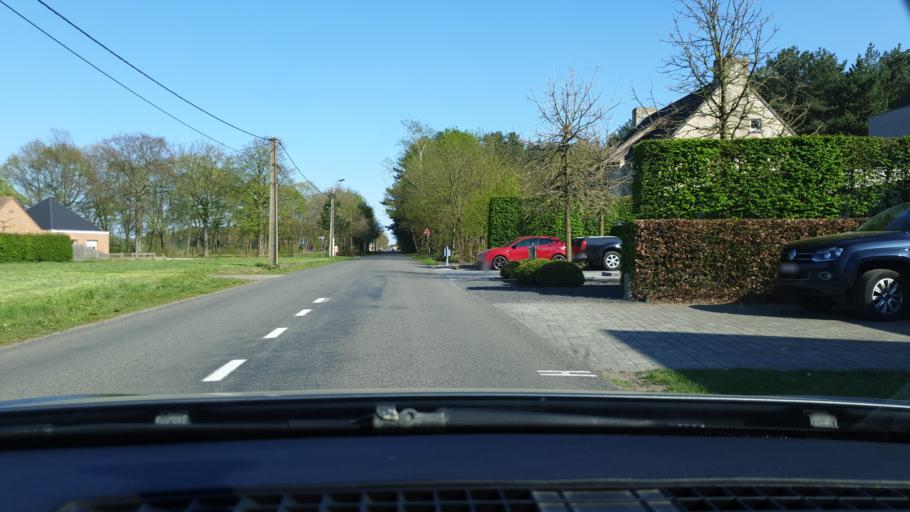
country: BE
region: Flanders
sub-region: Provincie Antwerpen
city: Olen
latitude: 51.1830
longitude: 4.9174
